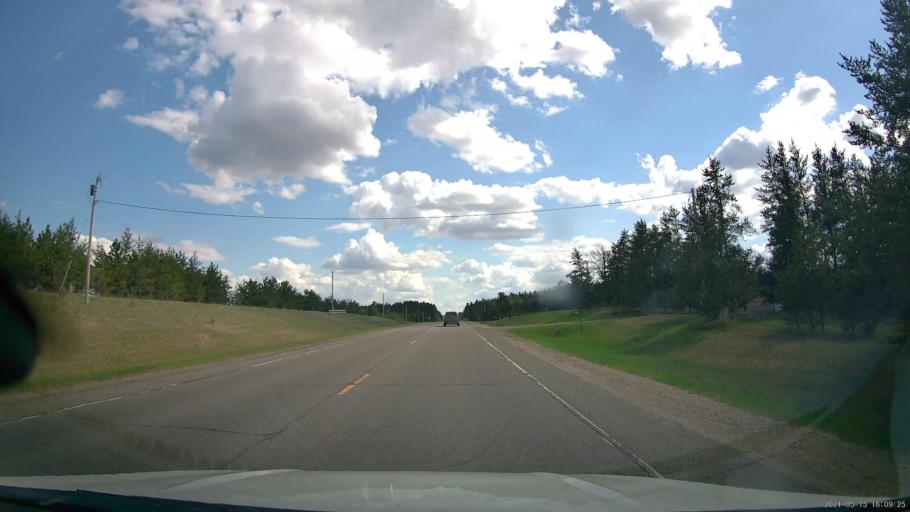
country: US
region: Minnesota
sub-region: Hubbard County
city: Park Rapids
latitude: 46.9498
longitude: -94.9528
